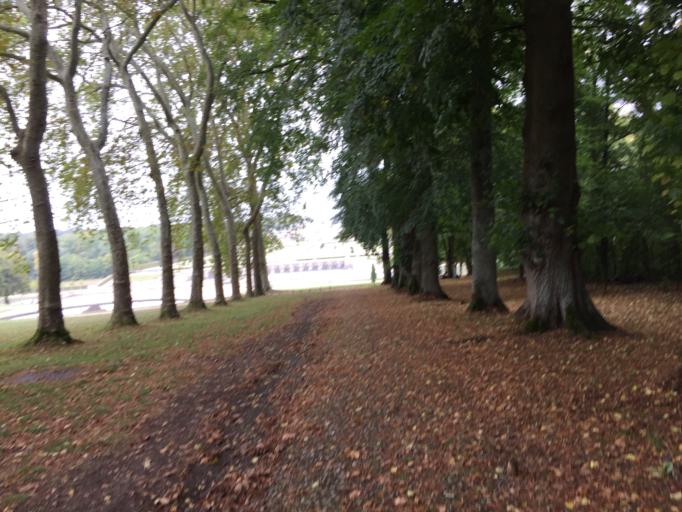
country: FR
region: Ile-de-France
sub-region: Departement de Seine-et-Marne
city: Maincy
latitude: 48.5579
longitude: 2.7161
